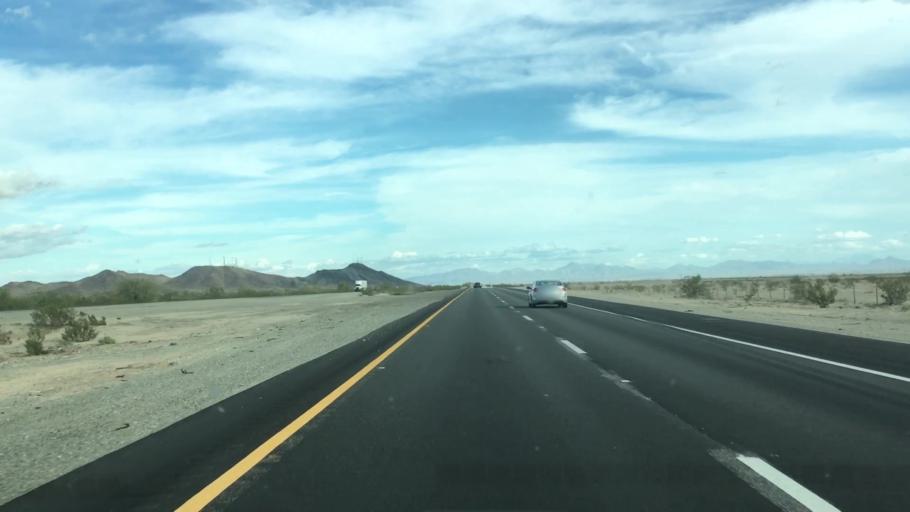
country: US
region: California
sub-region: Riverside County
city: Mesa Verde
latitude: 33.6097
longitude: -114.8074
